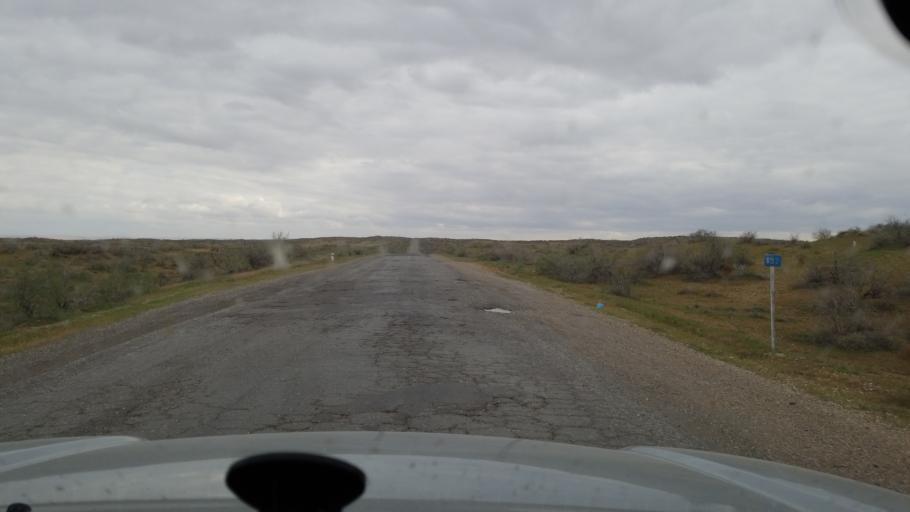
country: TM
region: Mary
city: Serhetabat
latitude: 36.1295
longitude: 62.6070
